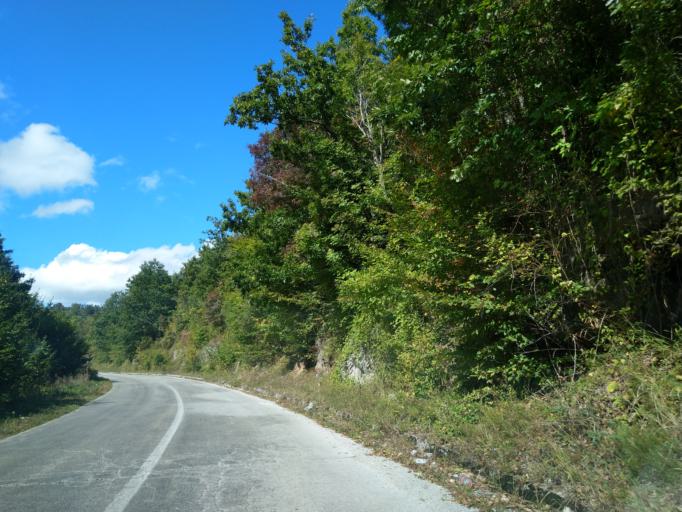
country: RS
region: Central Serbia
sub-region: Zlatiborski Okrug
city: Cajetina
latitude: 43.7121
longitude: 19.8361
